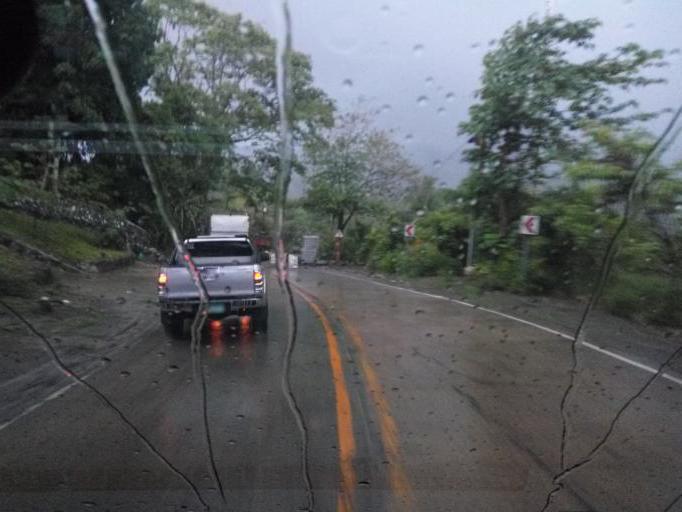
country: PH
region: Cagayan Valley
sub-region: Province of Nueva Vizcaya
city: Santa Fe
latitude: 16.1558
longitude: 120.9379
